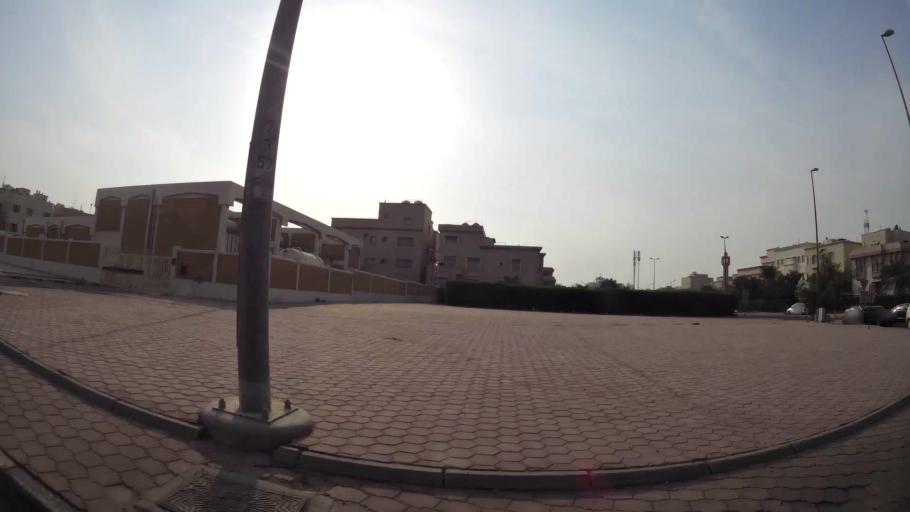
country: KW
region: Mubarak al Kabir
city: Sabah as Salim
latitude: 29.2370
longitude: 48.0618
